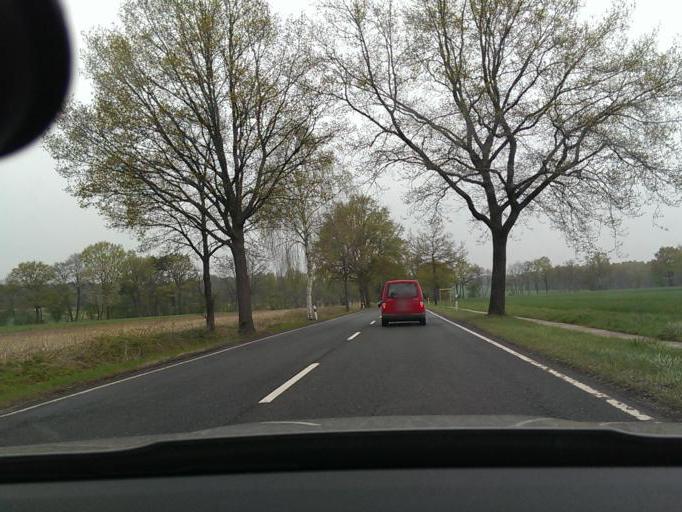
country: DE
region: Lower Saxony
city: Elze
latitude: 52.5279
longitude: 9.7265
